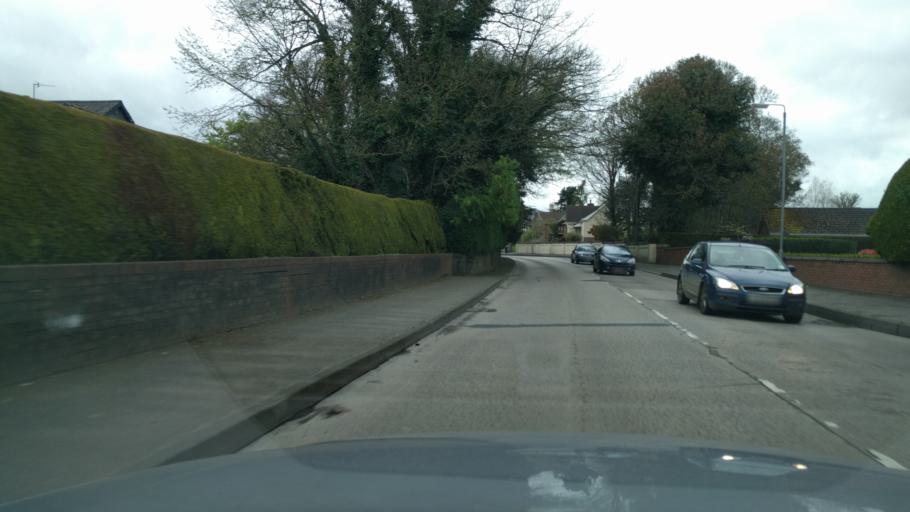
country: GB
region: Northern Ireland
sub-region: Down District
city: Warrenpoint
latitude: 54.1016
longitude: -6.2316
